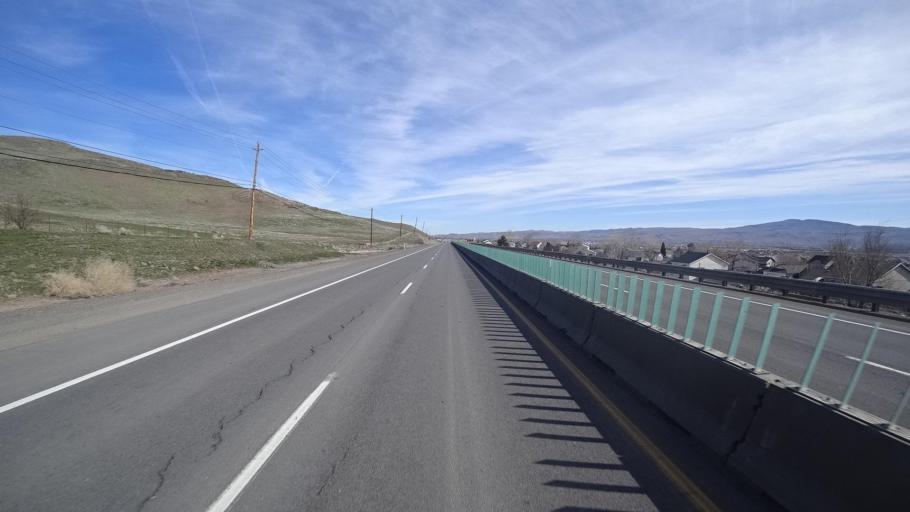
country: US
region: Nevada
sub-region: Washoe County
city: Sun Valley
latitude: 39.5990
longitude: -119.7364
